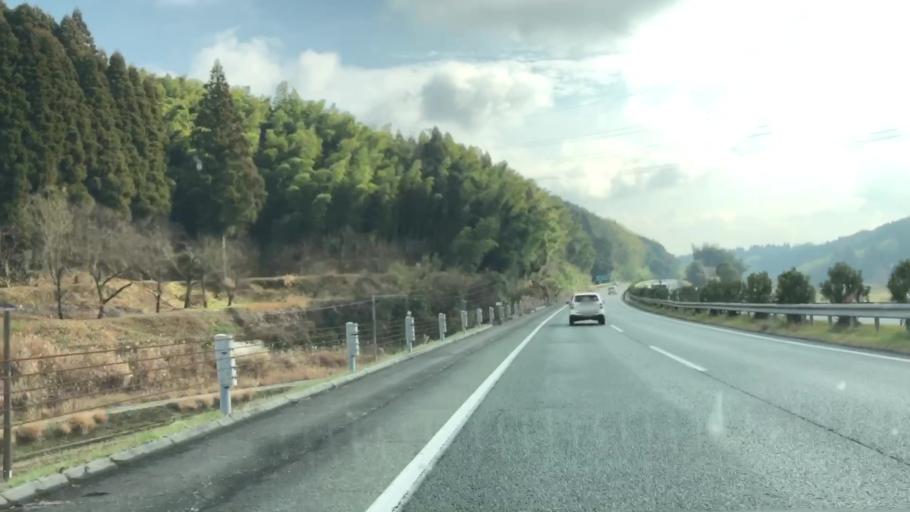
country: JP
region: Kumamoto
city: Yamaga
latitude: 33.0399
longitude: 130.5697
